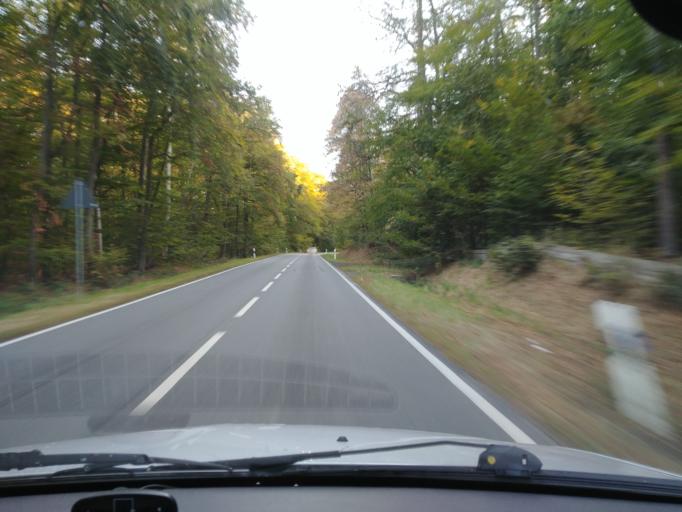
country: DE
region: Hesse
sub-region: Regierungsbezirk Darmstadt
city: Waldems
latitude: 50.2620
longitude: 8.3241
